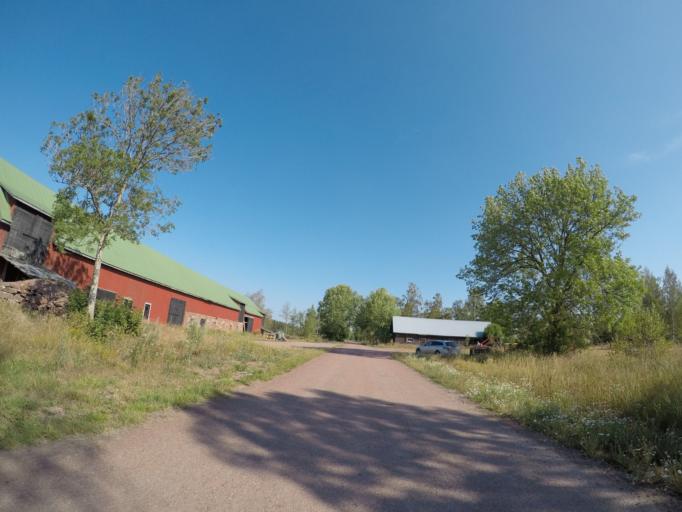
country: AX
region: Alands landsbygd
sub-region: Finstroem
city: Finstroem
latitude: 60.2775
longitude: 19.9573
